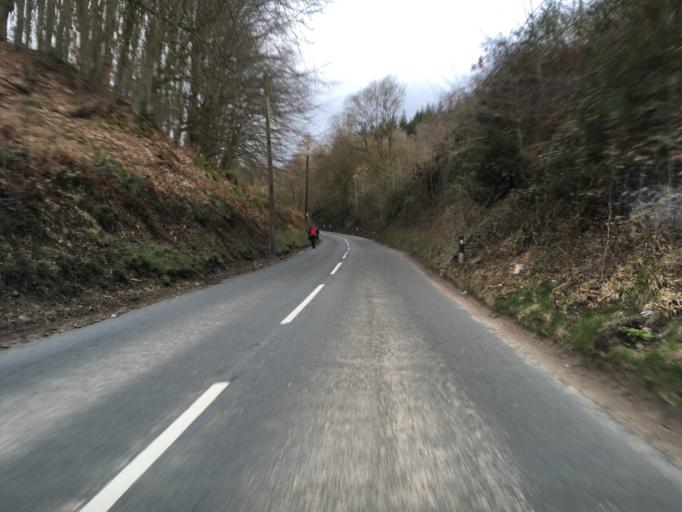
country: GB
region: England
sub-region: Gloucestershire
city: Coleford
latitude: 51.7996
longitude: -2.5844
